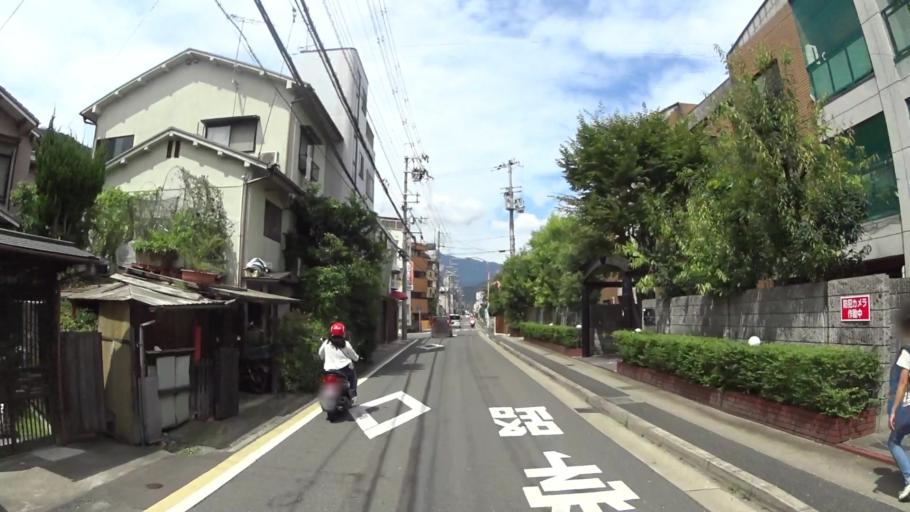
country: JP
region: Kyoto
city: Muko
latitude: 35.0035
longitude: 135.6853
